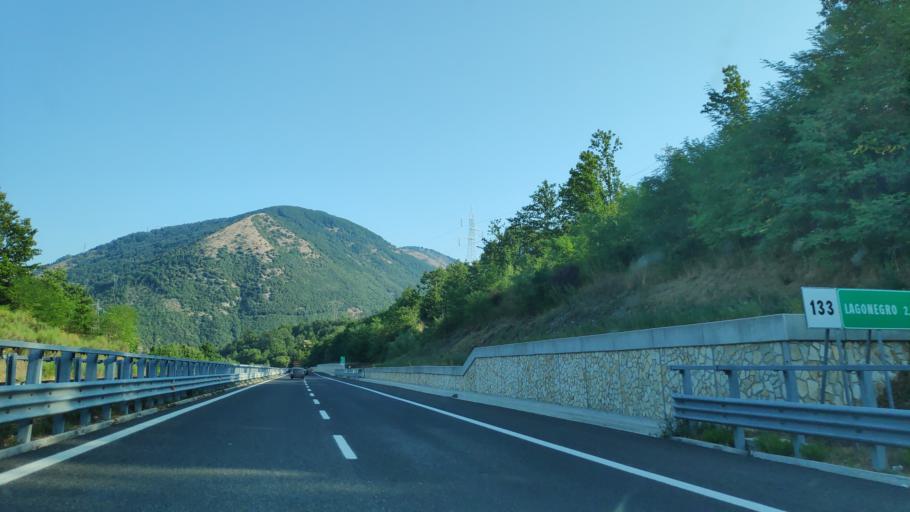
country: IT
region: Basilicate
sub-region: Provincia di Potenza
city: Lagonegro
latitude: 40.1178
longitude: 15.7847
